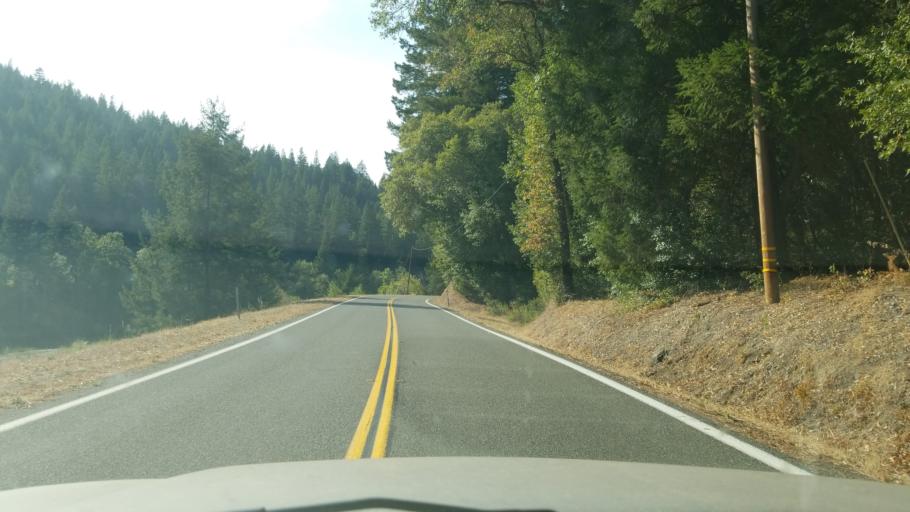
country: US
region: California
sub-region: Humboldt County
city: Redway
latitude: 40.1960
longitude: -123.7722
